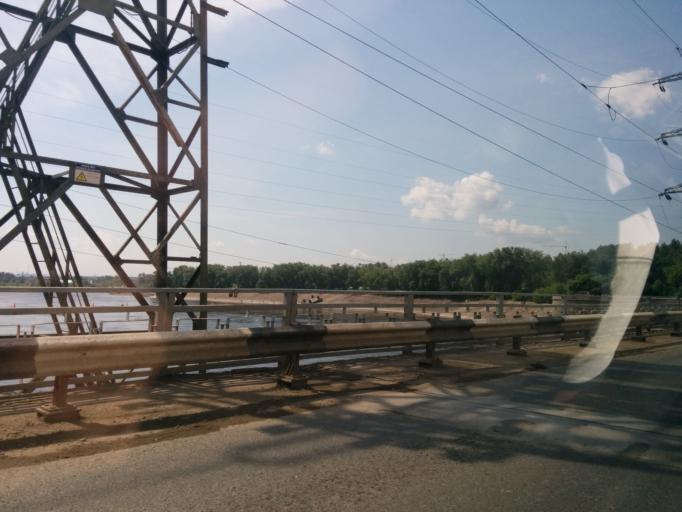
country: RU
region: Perm
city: Perm
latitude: 58.1144
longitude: 56.3285
